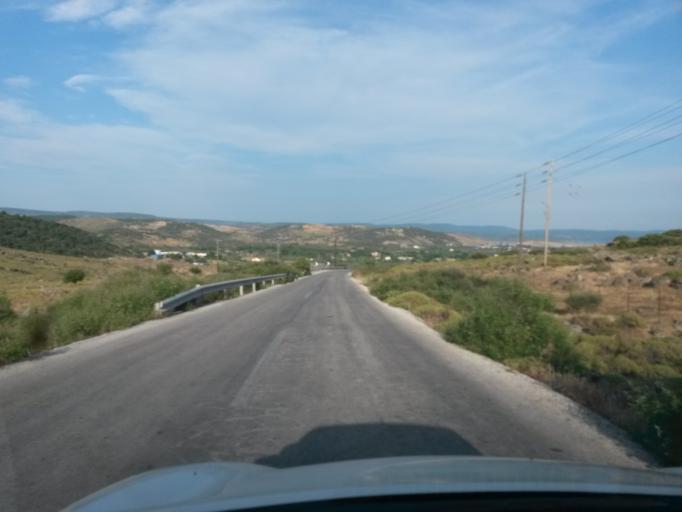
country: GR
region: North Aegean
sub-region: Nomos Lesvou
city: Kalloni
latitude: 39.2448
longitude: 26.1915
